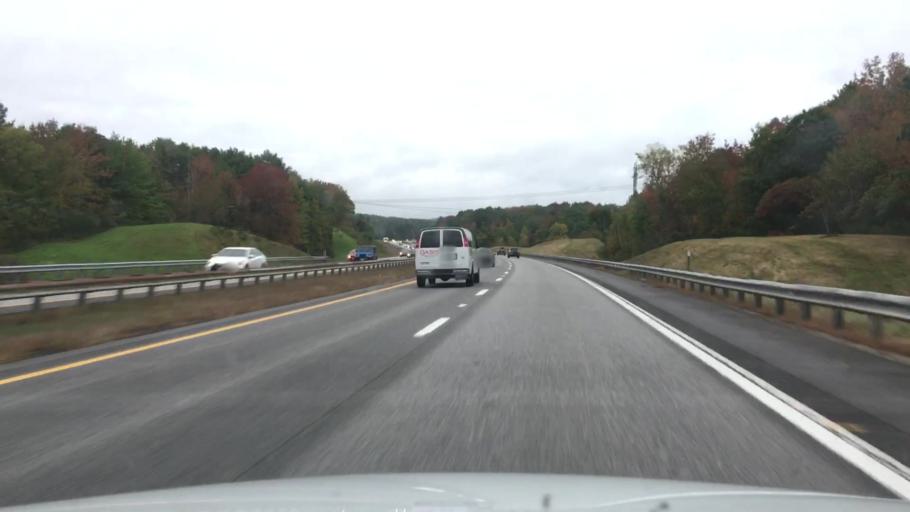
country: US
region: Maine
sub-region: Cumberland County
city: Cumberland Center
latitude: 43.7552
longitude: -70.3048
